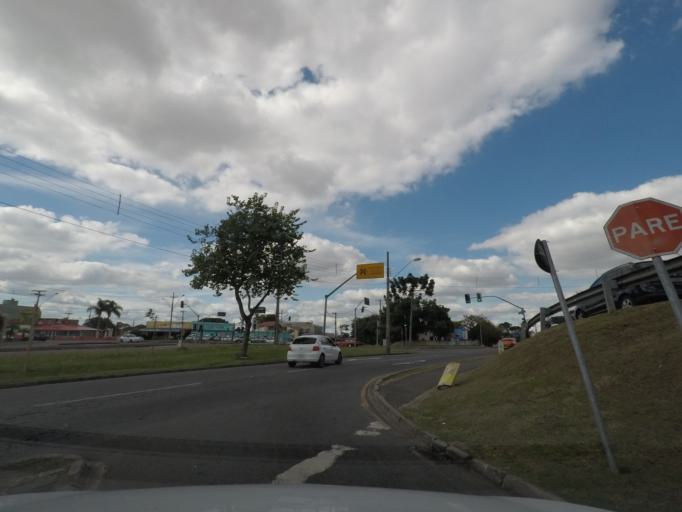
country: BR
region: Parana
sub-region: Pinhais
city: Pinhais
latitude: -25.4422
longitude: -49.2326
